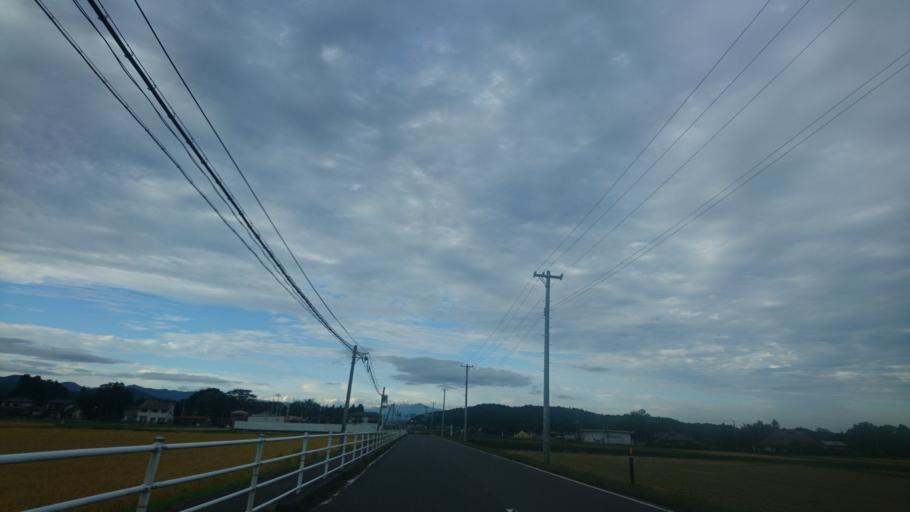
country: JP
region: Fukushima
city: Sukagawa
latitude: 37.3179
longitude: 140.2672
